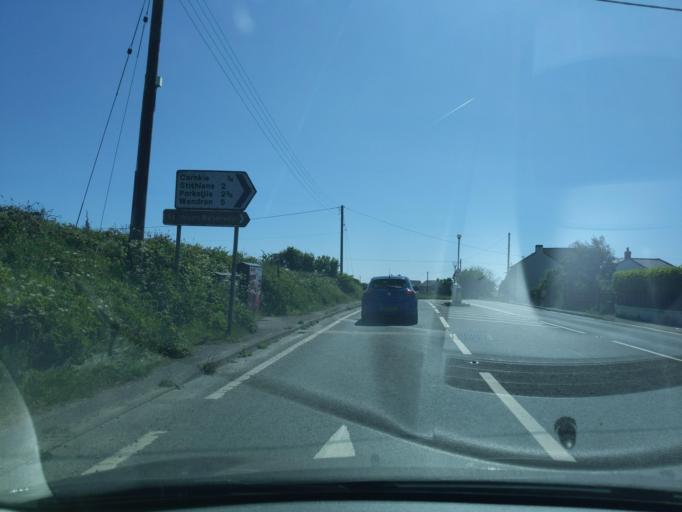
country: GB
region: England
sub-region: Cornwall
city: Wendron
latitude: 50.1618
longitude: -5.1838
